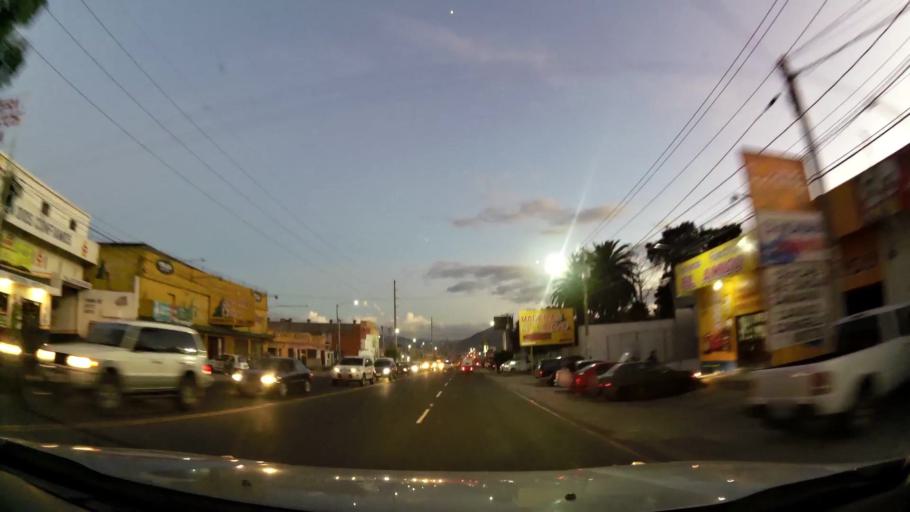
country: GT
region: Guatemala
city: Villa Nueva
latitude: 14.5120
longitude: -90.5728
